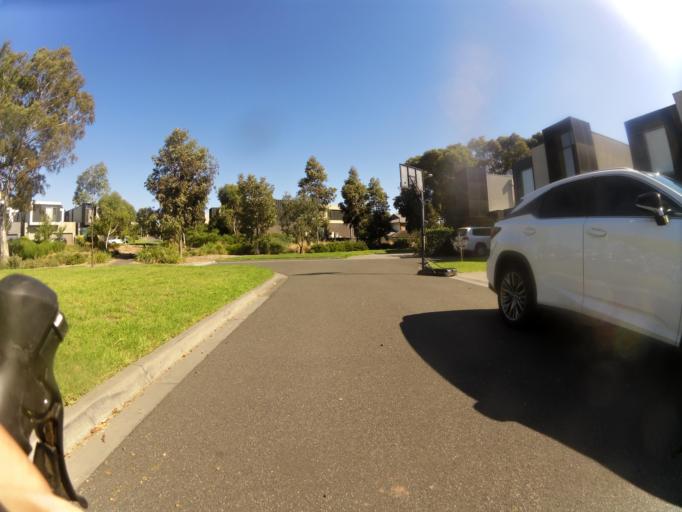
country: AU
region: Victoria
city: Alphington
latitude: -37.7944
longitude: 145.0278
